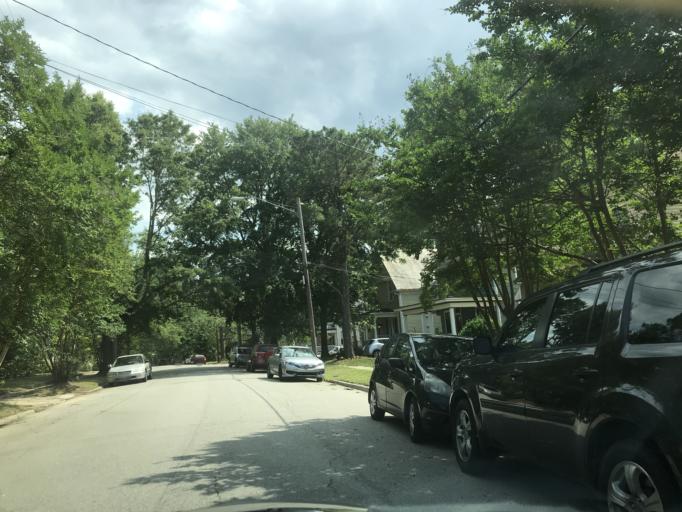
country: US
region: North Carolina
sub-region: Wake County
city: Raleigh
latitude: 35.7763
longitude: -78.6520
